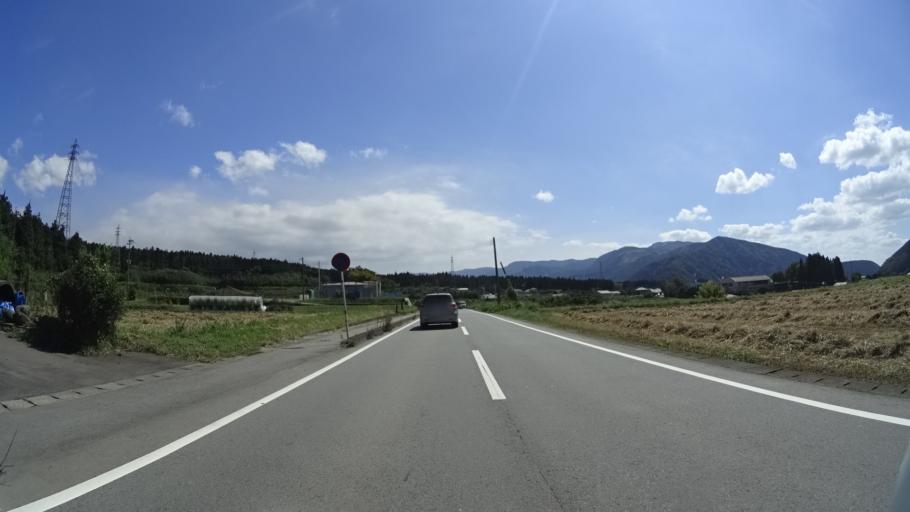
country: JP
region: Kumamoto
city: Aso
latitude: 32.8883
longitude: 130.9953
